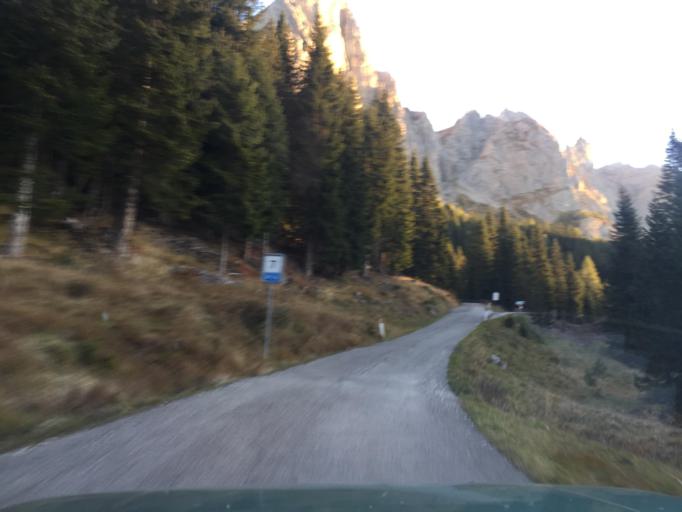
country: IT
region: Veneto
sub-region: Provincia di Belluno
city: Granvilla
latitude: 46.6153
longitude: 12.7233
